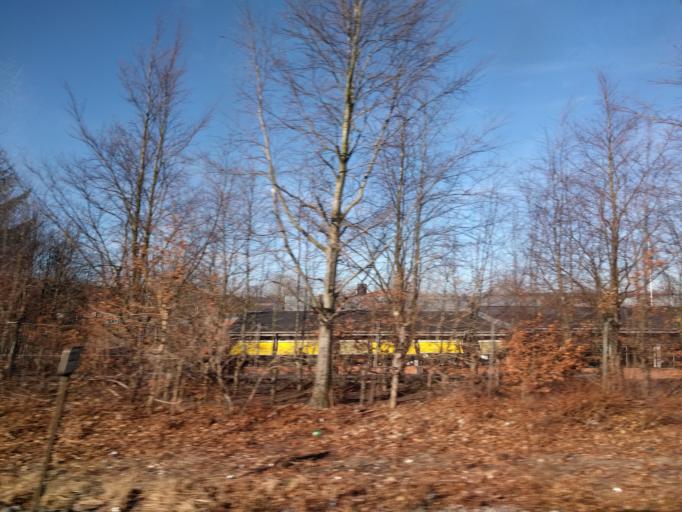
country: DK
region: Capital Region
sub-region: Rudersdal Kommune
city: Trorod
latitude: 55.8513
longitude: 12.5614
